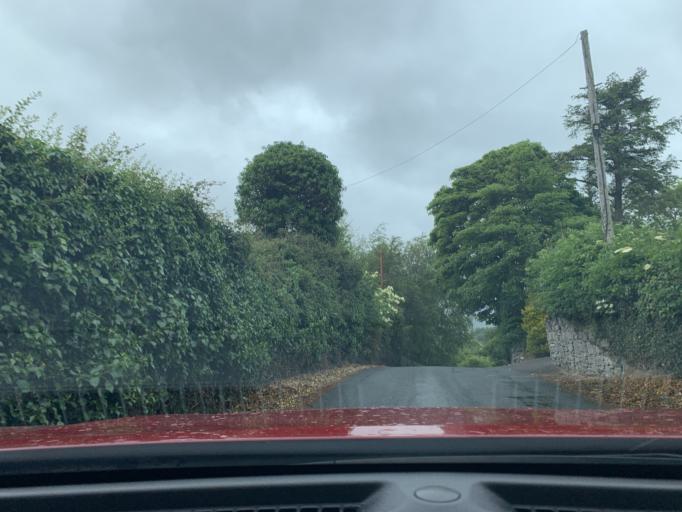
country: IE
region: Connaught
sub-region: Sligo
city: Sligo
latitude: 54.2936
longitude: -8.4634
